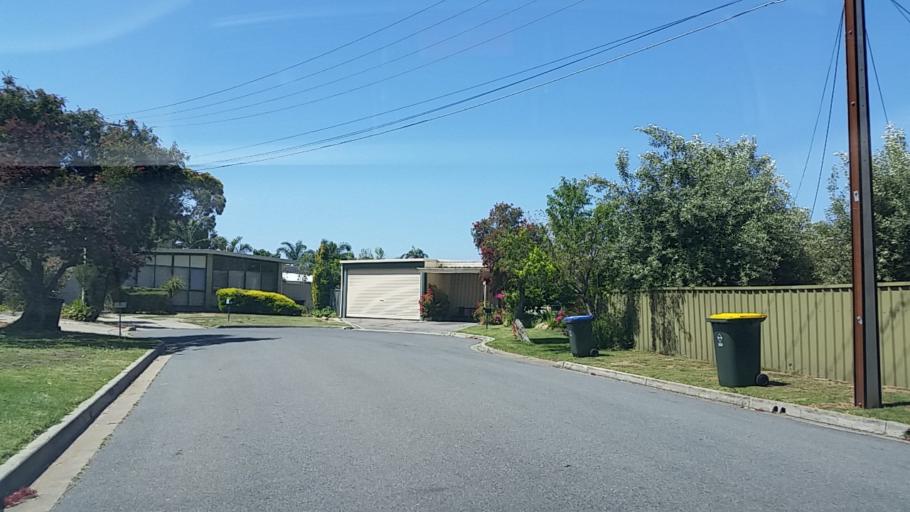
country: AU
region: South Australia
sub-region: Charles Sturt
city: Grange
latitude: -34.9014
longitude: 138.4987
